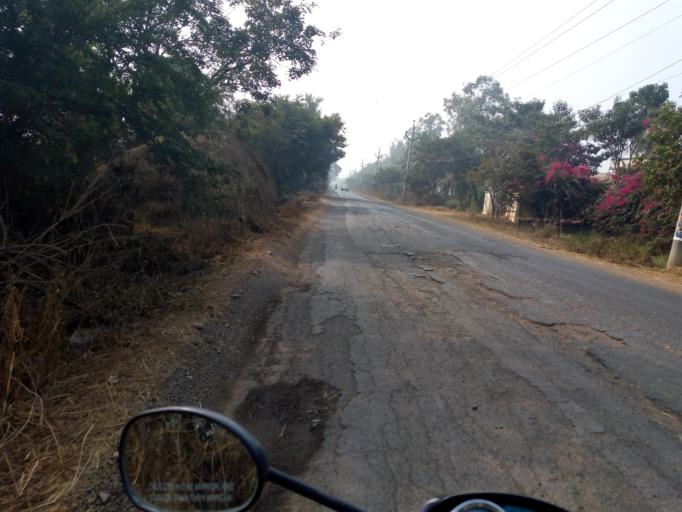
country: IN
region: Andhra Pradesh
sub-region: West Godavari
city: Tadepallegudem
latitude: 16.7648
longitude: 81.4248
